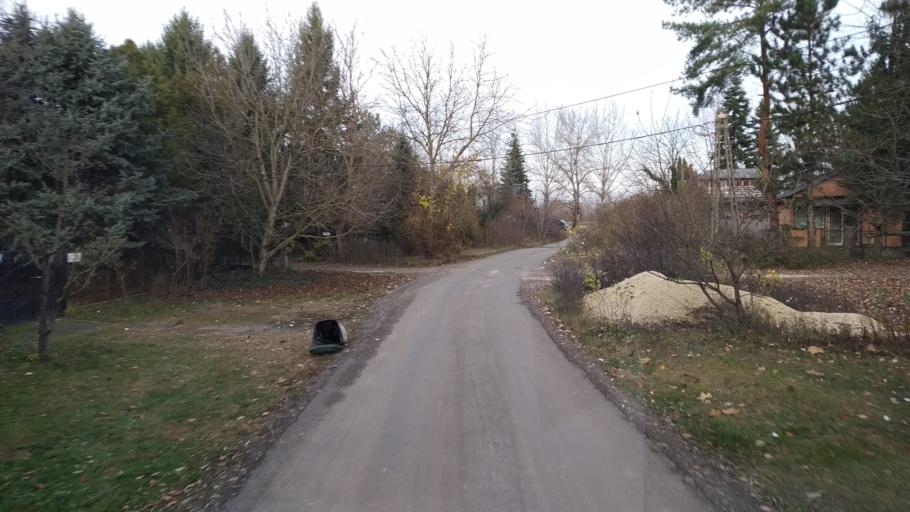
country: HU
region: Pest
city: God
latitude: 47.6844
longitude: 19.1141
